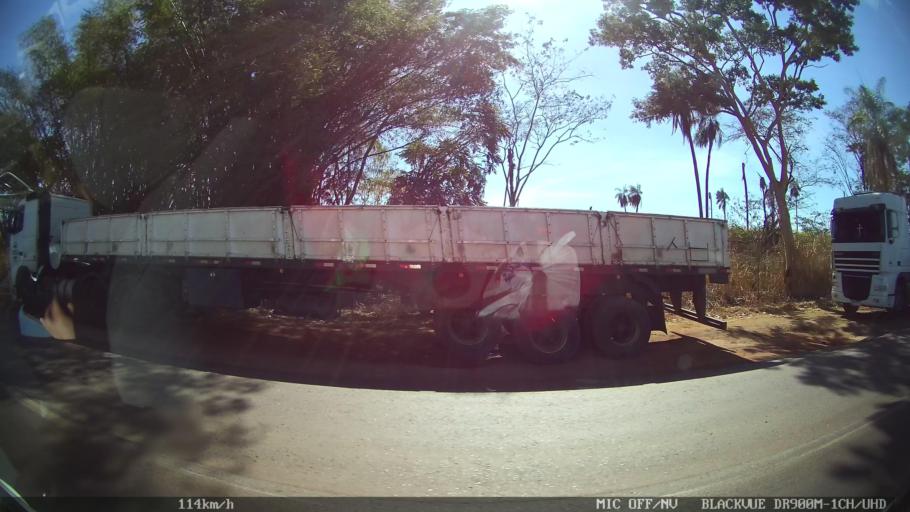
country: BR
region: Sao Paulo
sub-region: Barretos
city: Barretos
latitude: -20.4995
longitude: -48.5387
